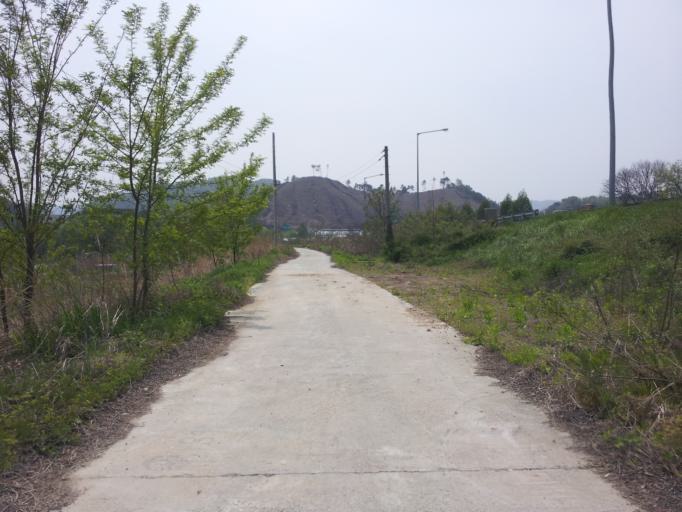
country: KR
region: Daejeon
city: Daejeon
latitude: 36.2592
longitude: 127.2826
